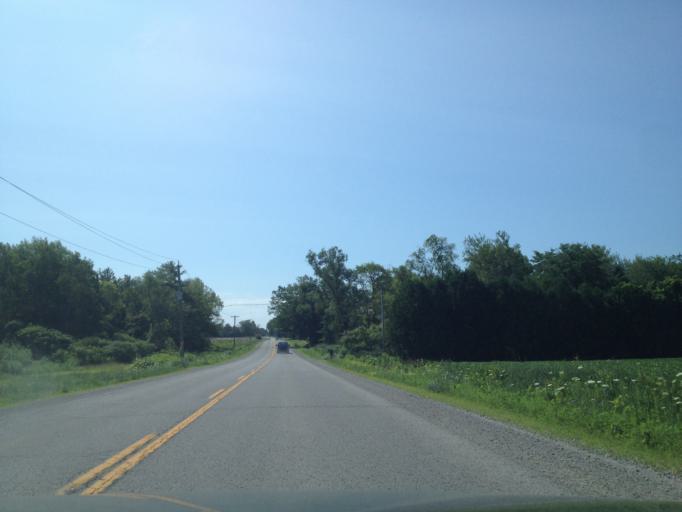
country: CA
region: Ontario
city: Norfolk County
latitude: 42.7818
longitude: -80.4024
